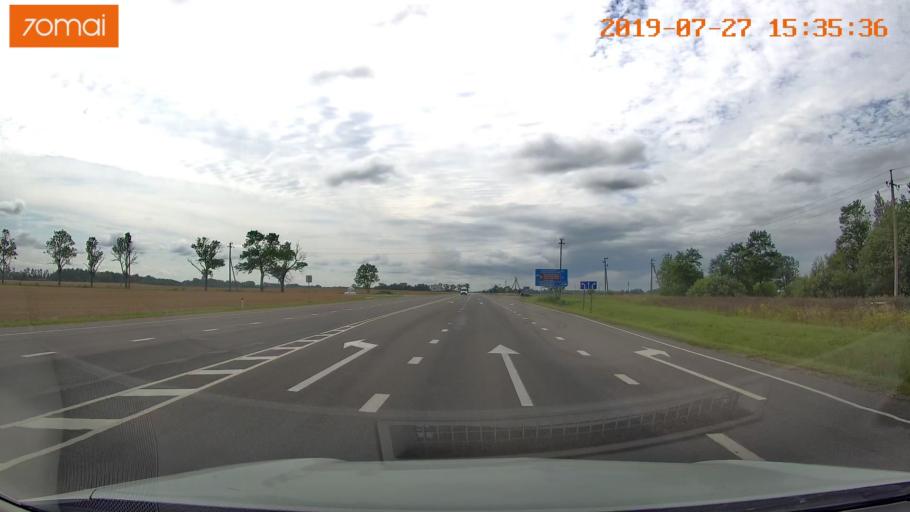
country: RU
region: Kaliningrad
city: Nesterov
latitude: 54.6134
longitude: 22.3929
